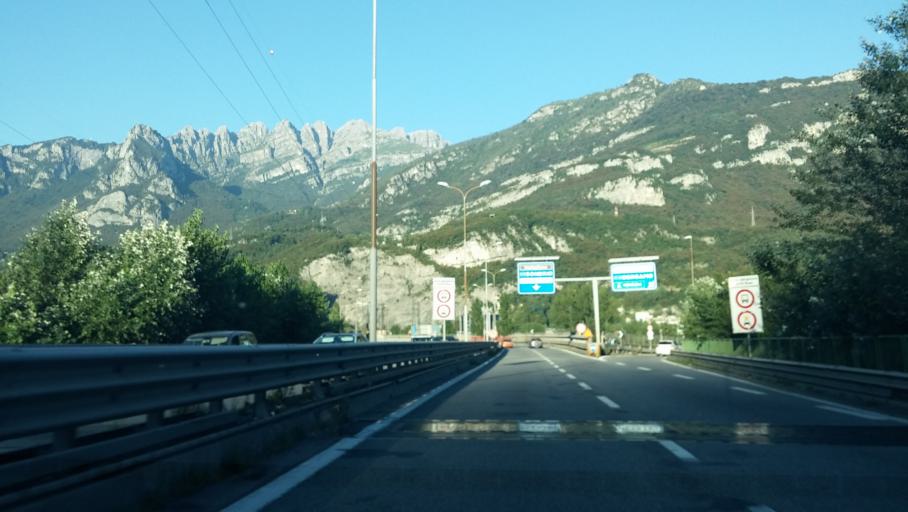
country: IT
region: Lombardy
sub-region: Provincia di Lecco
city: Pescate
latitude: 45.8391
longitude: 9.4015
